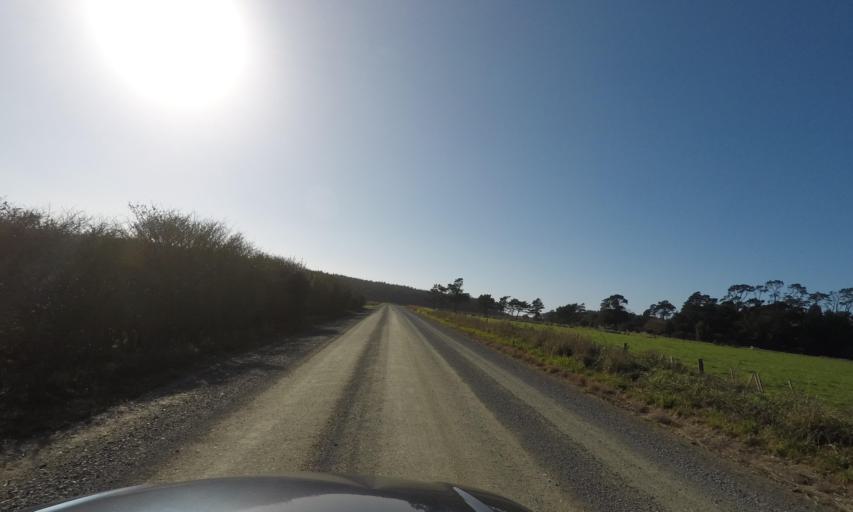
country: NZ
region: Auckland
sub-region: Auckland
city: Wellsford
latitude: -36.1570
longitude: 174.6154
